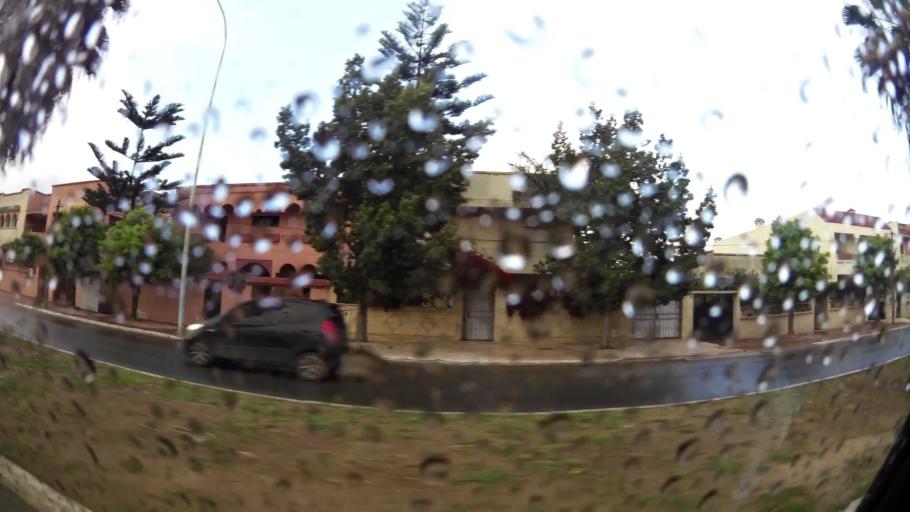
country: MA
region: Doukkala-Abda
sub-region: El-Jadida
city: El Jadida
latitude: 33.2326
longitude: -8.5005
